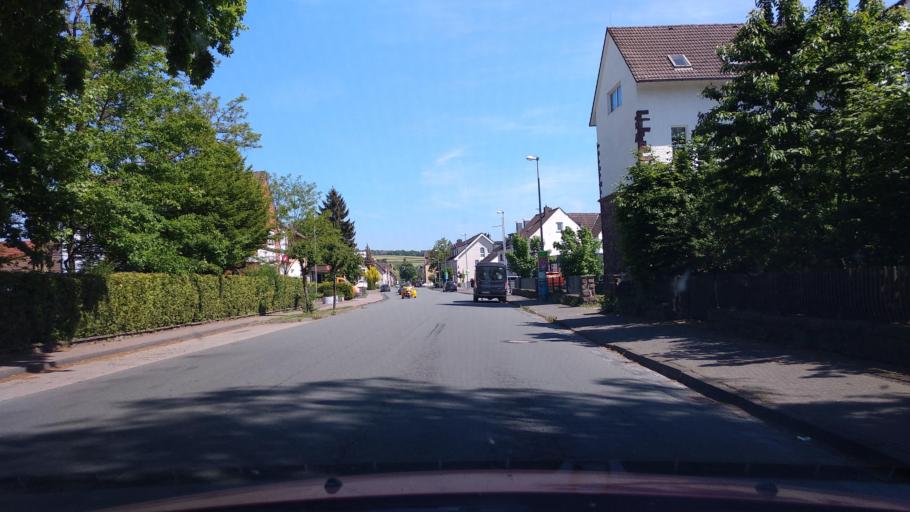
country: DE
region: North Rhine-Westphalia
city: Beverungen
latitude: 51.6609
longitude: 9.3833
